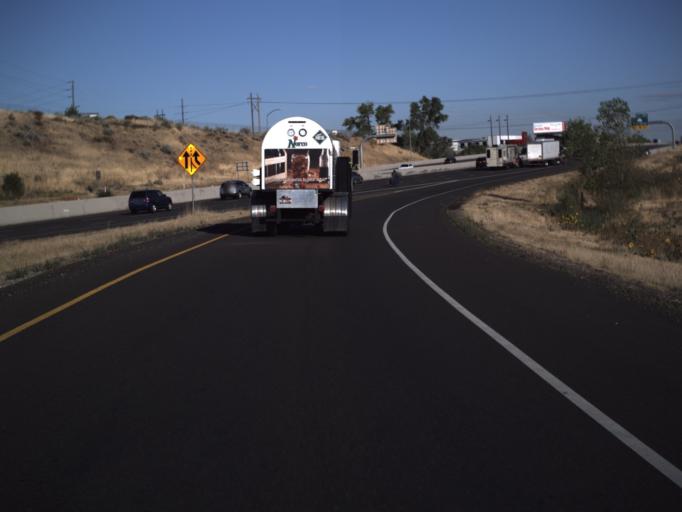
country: US
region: Utah
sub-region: Weber County
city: Ogden
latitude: 41.2075
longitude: -111.9945
